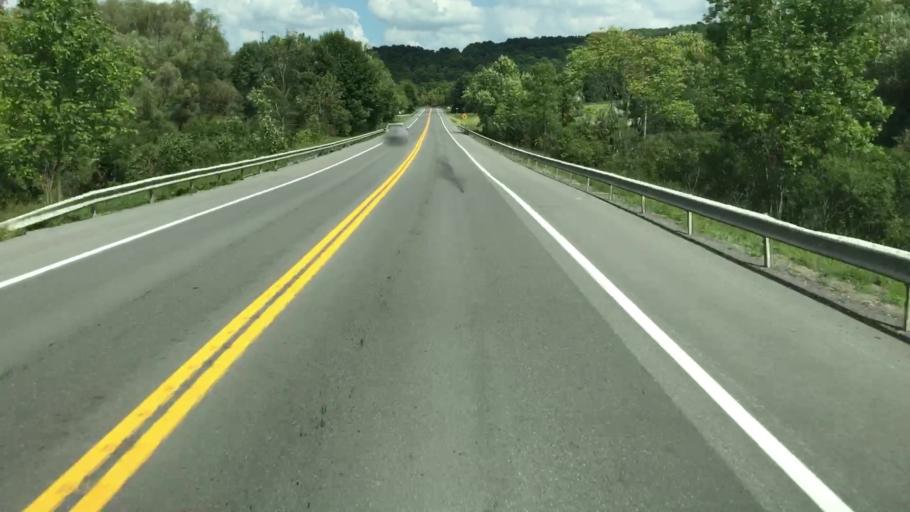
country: US
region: New York
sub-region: Onondaga County
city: Marcellus
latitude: 42.9559
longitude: -76.3422
